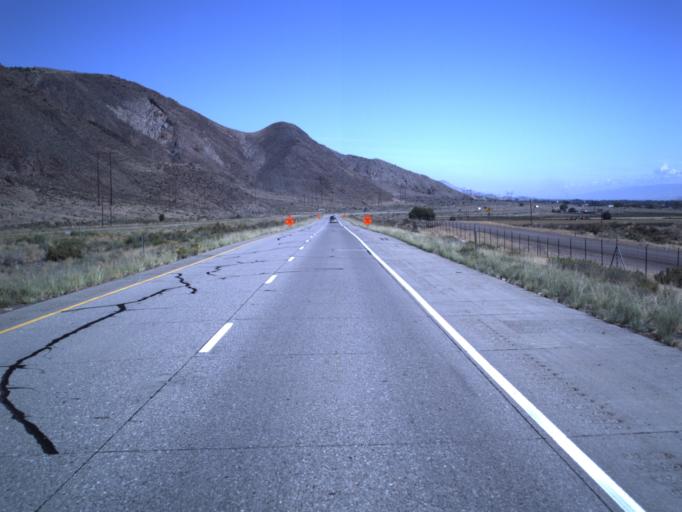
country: US
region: Utah
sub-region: Sevier County
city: Richfield
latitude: 38.7185
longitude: -112.1330
